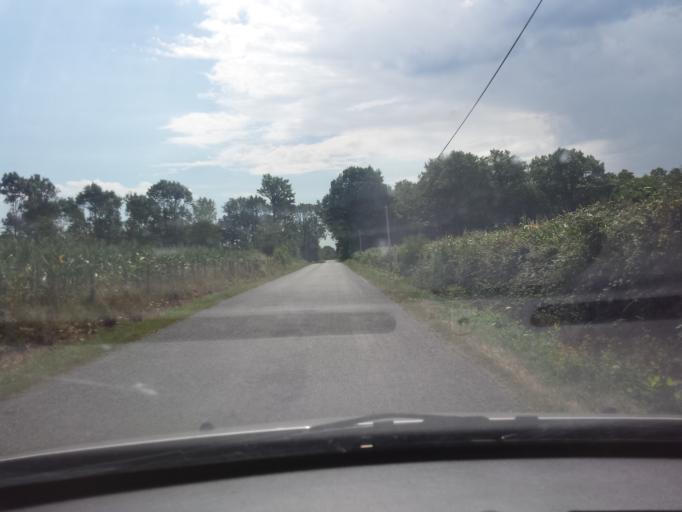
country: FR
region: Poitou-Charentes
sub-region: Departement de la Vienne
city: Availles-Limouzine
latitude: 46.0797
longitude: 0.7435
